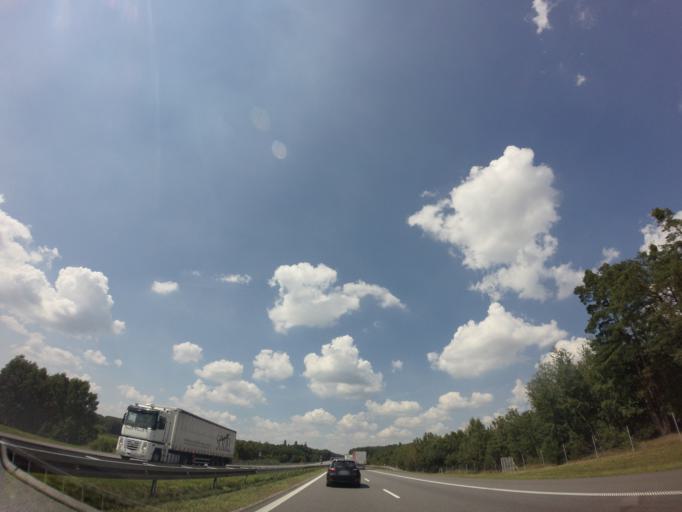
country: PL
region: Opole Voivodeship
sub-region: Powiat opolski
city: Proszkow
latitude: 50.5800
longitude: 17.8350
